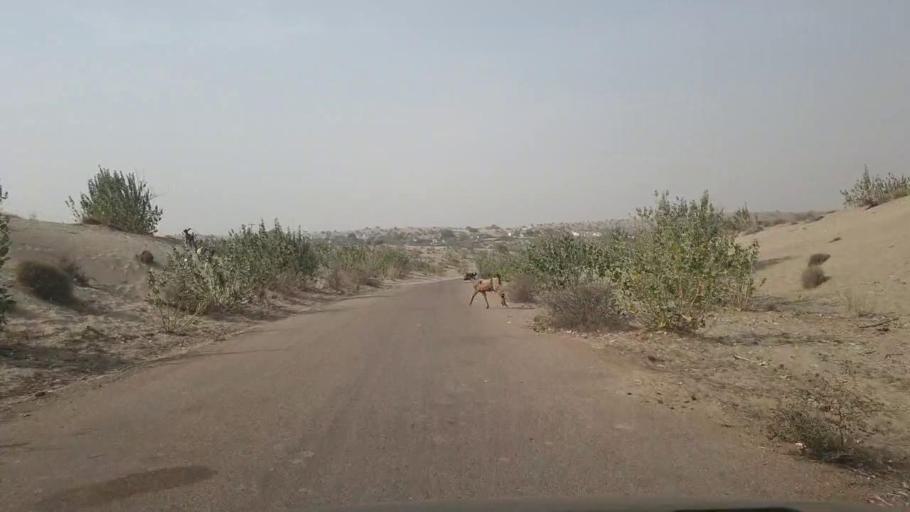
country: PK
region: Sindh
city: Chor
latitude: 25.6172
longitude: 69.9290
